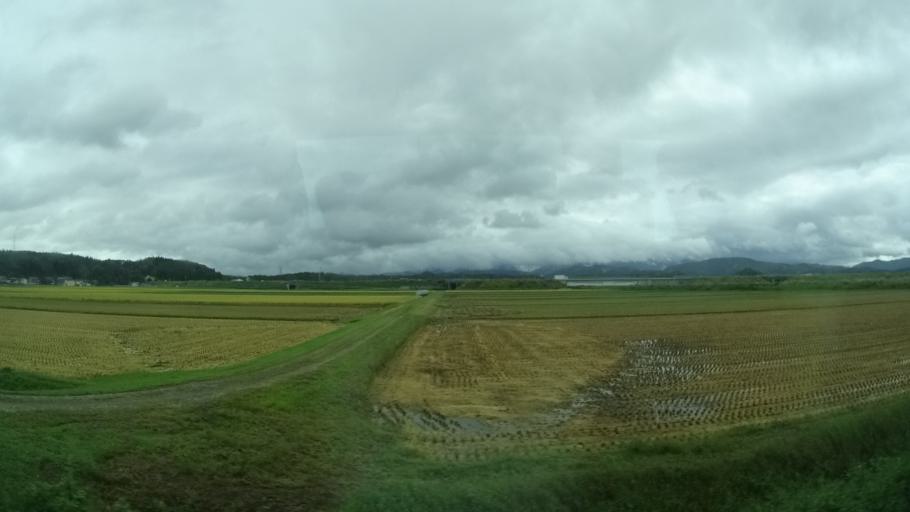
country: JP
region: Niigata
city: Murakami
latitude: 38.1991
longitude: 139.4601
